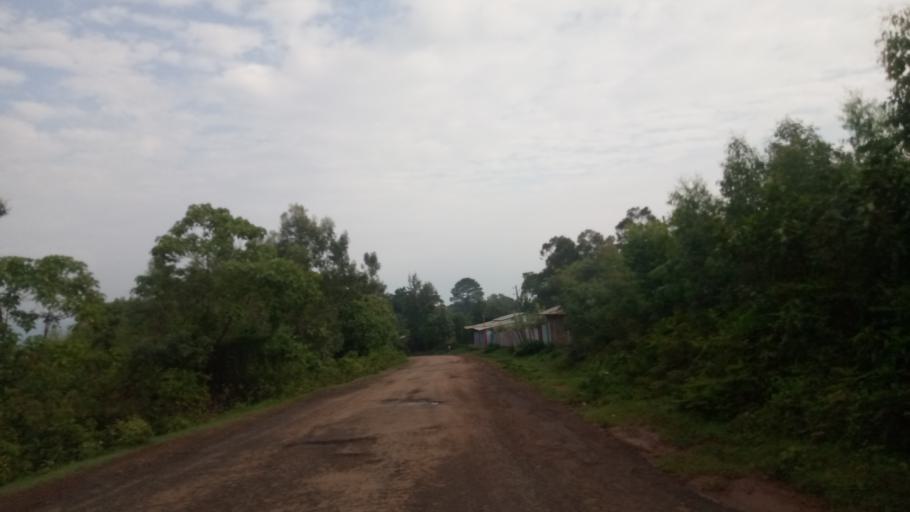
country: ET
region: Oromiya
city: Agaro
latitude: 7.7961
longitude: 36.7218
